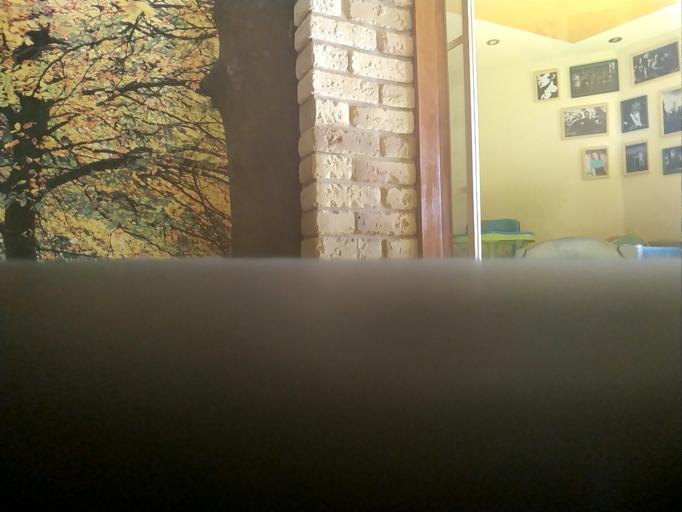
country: RU
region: Smolensk
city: Temkino
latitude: 55.0441
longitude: 34.9209
